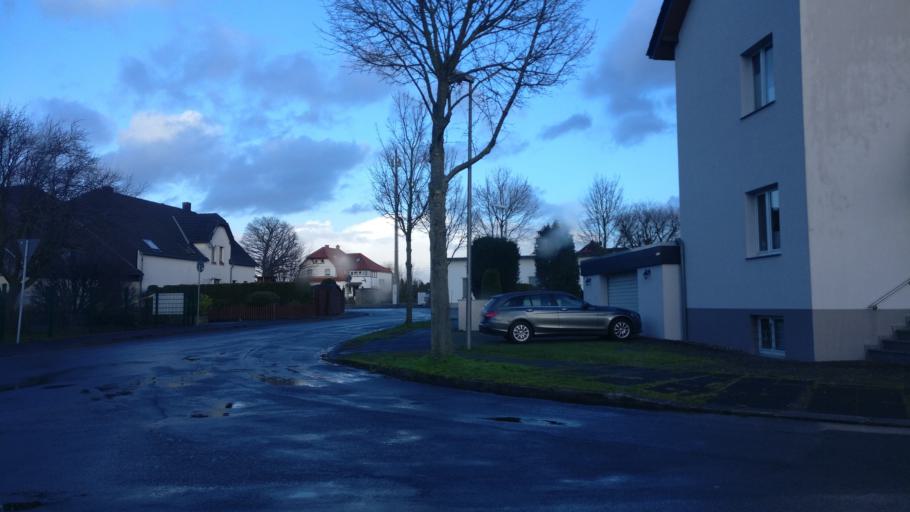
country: DE
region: North Rhine-Westphalia
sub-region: Regierungsbezirk Detmold
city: Lage
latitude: 52.0268
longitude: 8.7641
